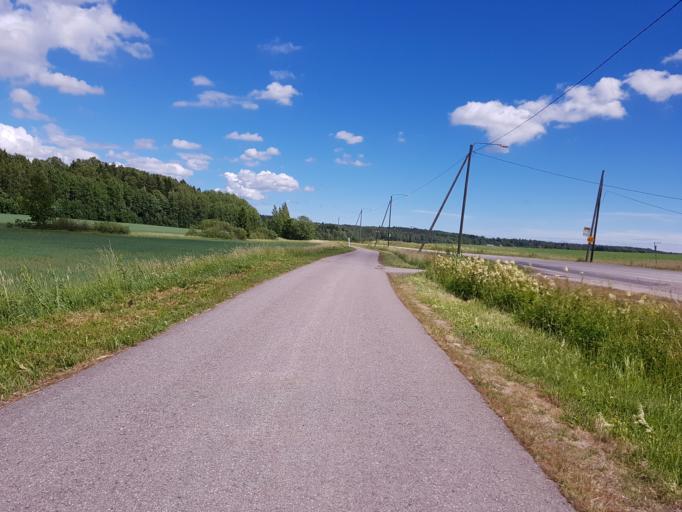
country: FI
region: Uusimaa
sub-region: Helsinki
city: Nurmijaervi
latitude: 60.3477
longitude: 24.8835
